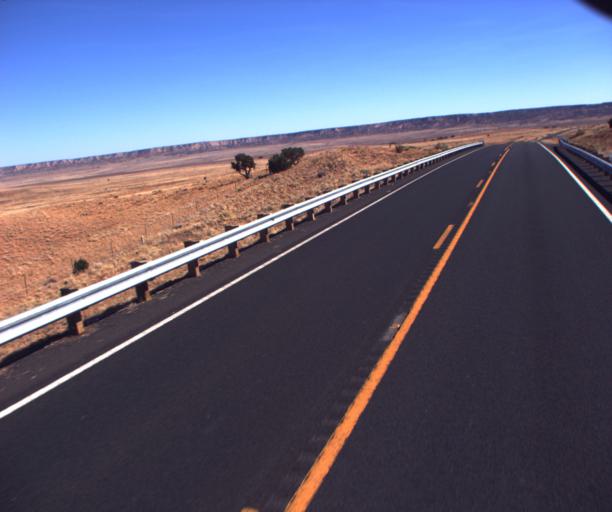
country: US
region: Arizona
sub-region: Apache County
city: Ganado
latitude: 35.7831
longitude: -109.6647
